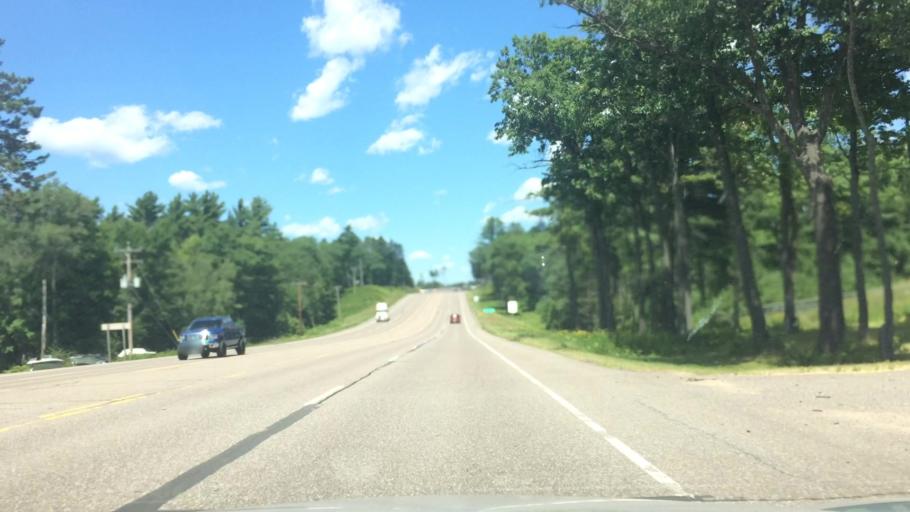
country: US
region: Wisconsin
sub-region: Vilas County
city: Lac du Flambeau
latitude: 45.8452
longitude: -89.7054
